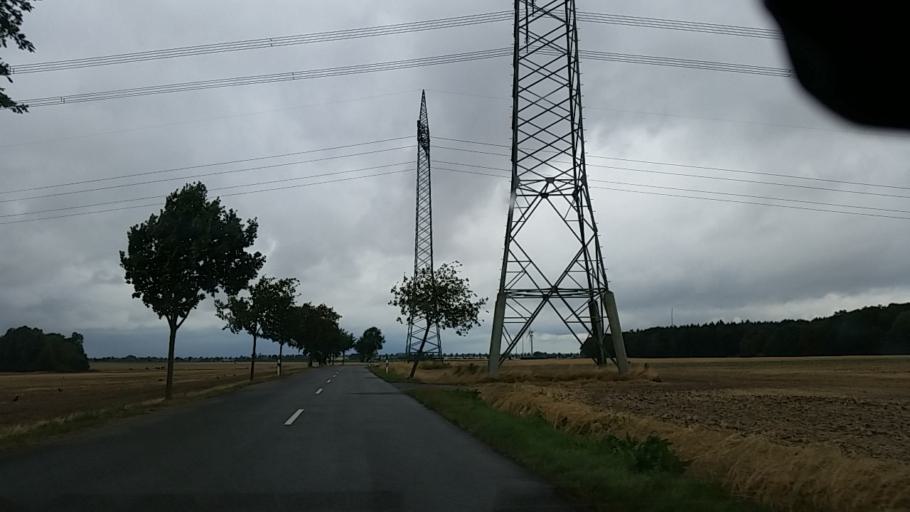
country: DE
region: Lower Saxony
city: Lehre
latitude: 52.3755
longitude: 10.6670
